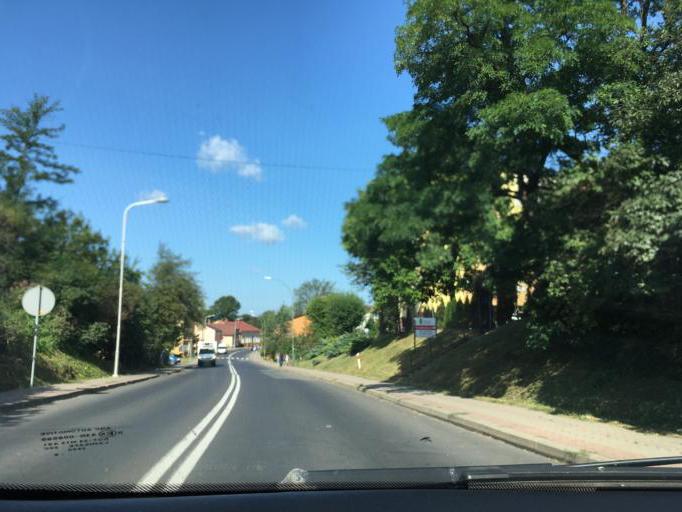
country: PL
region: Subcarpathian Voivodeship
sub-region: Powiat leski
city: Lesko
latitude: 49.4662
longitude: 22.3349
